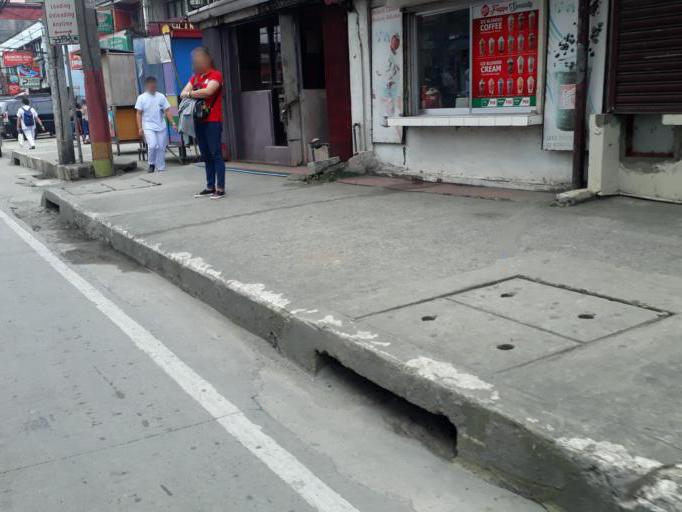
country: PH
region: Calabarzon
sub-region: Province of Rizal
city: Valenzuela
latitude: 14.6779
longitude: 120.9802
